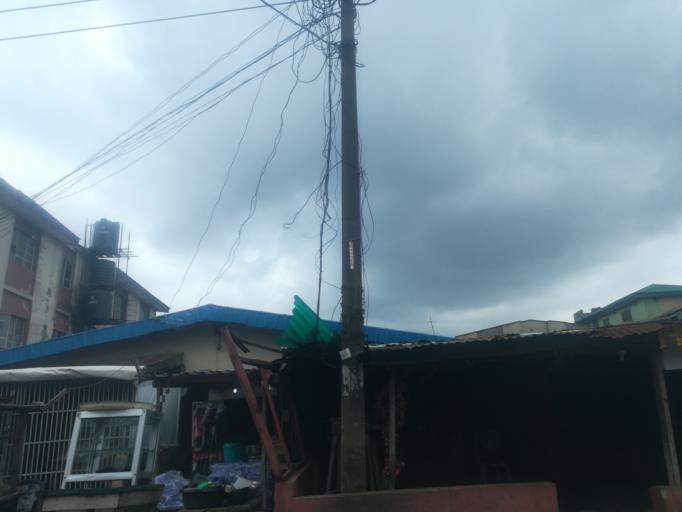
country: NG
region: Lagos
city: Somolu
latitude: 6.5548
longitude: 3.3922
